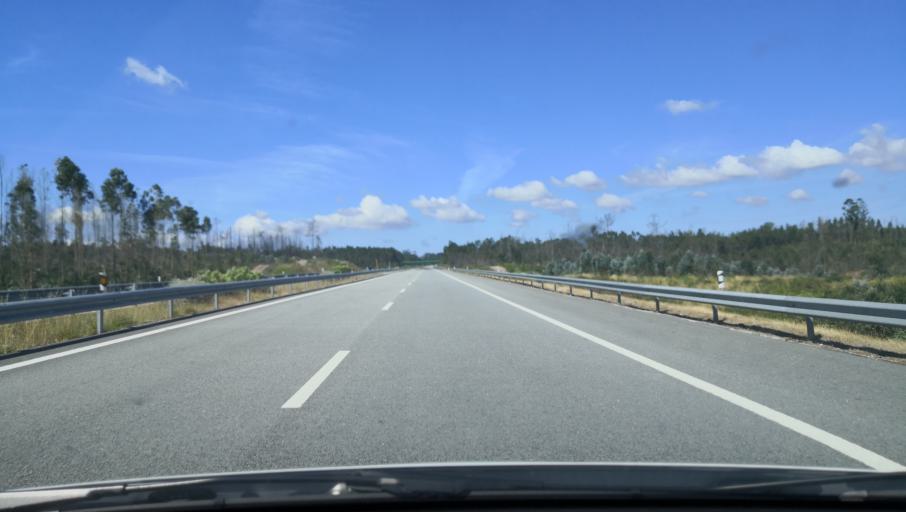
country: PT
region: Coimbra
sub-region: Cantanhede
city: Cantanhede
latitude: 40.2830
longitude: -8.5798
